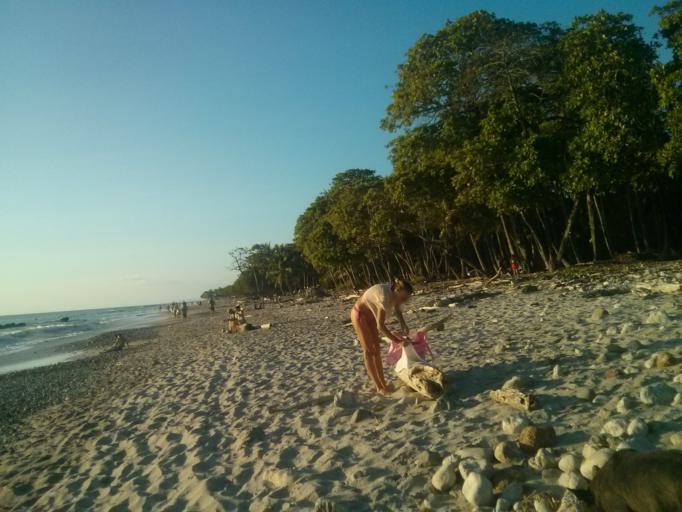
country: CR
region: Guanacaste
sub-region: Canton de Nandayure
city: Bejuco
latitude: 9.6299
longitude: -85.1558
